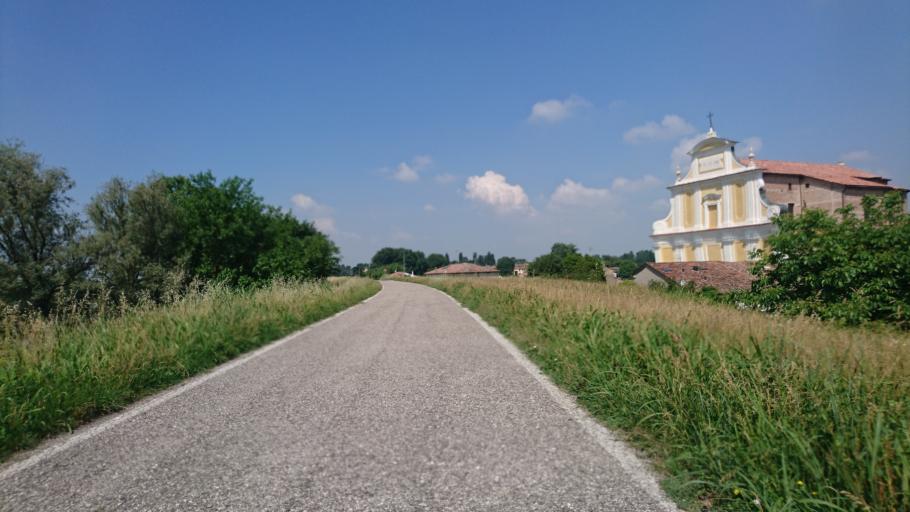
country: IT
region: Lombardy
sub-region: Provincia di Mantova
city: San Benedetto Po
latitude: 45.0819
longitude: 10.9624
